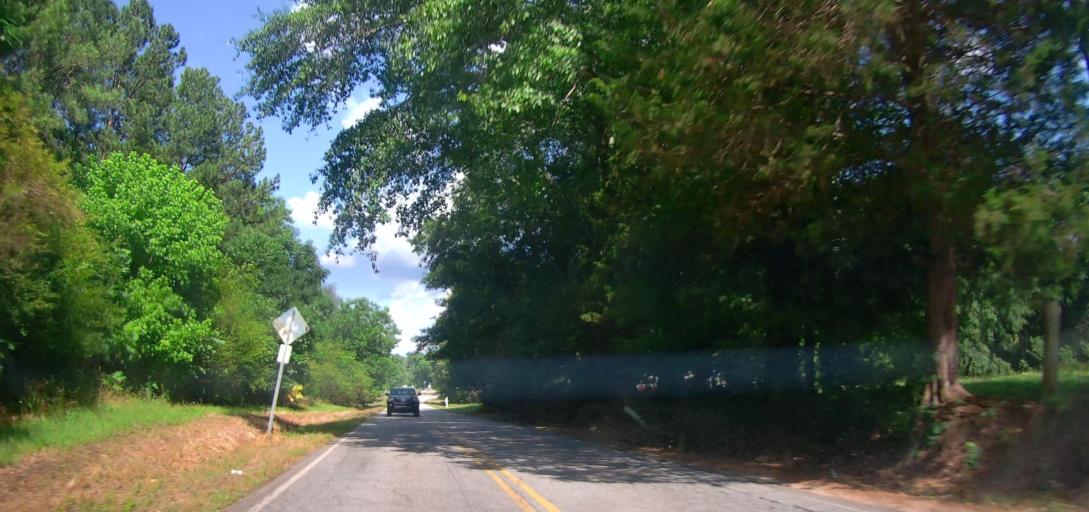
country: US
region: Georgia
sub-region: Spalding County
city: East Griffin
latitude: 33.2328
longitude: -84.1442
